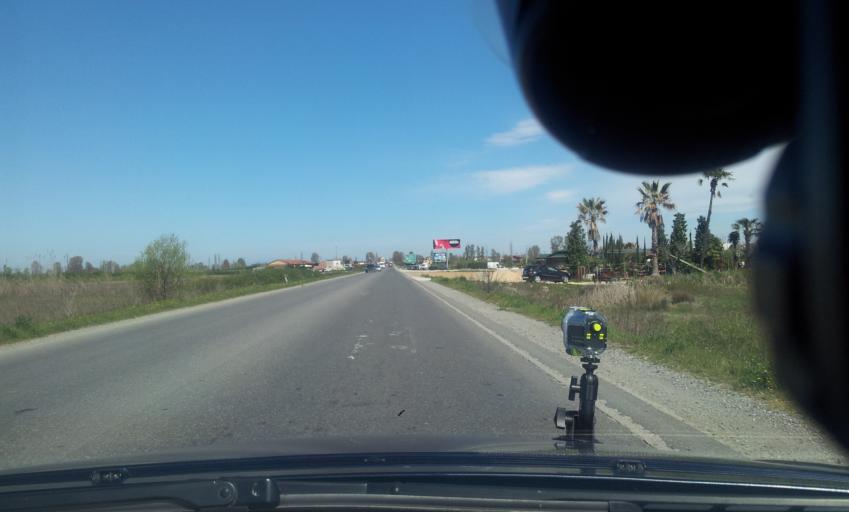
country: AL
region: Durres
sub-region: Rrethi i Krujes
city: Thumane
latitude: 41.5336
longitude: 19.6794
